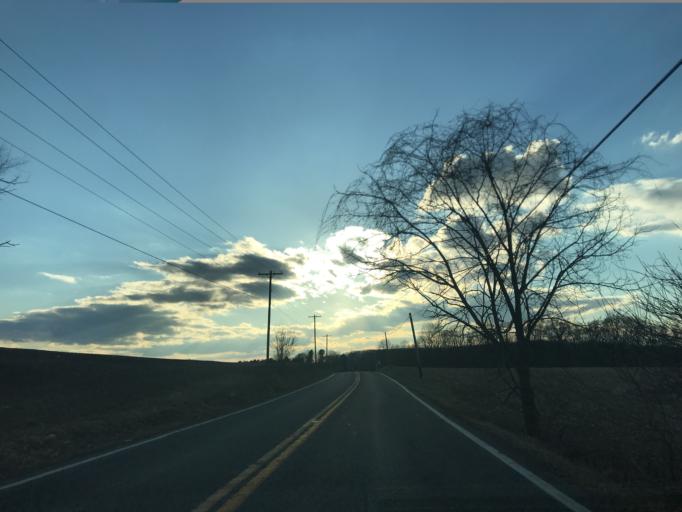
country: US
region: Pennsylvania
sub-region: York County
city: Susquehanna Trails
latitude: 39.7188
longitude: -76.3880
